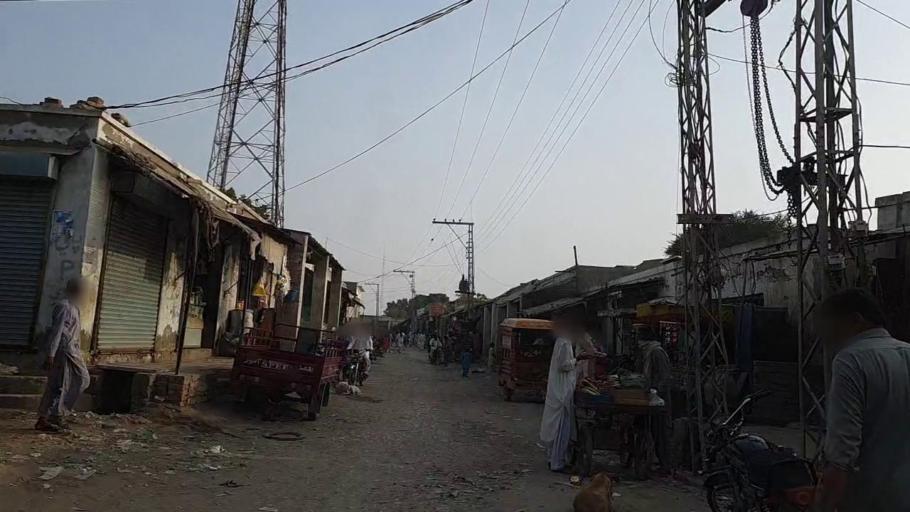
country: PK
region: Sindh
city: Naukot
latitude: 24.6585
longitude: 69.2896
